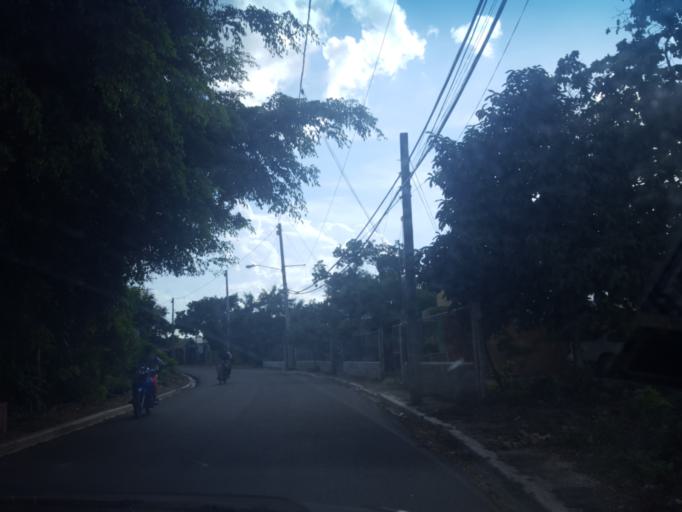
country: DO
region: Santiago
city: Licey al Medio
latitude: 19.3745
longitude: -70.6239
